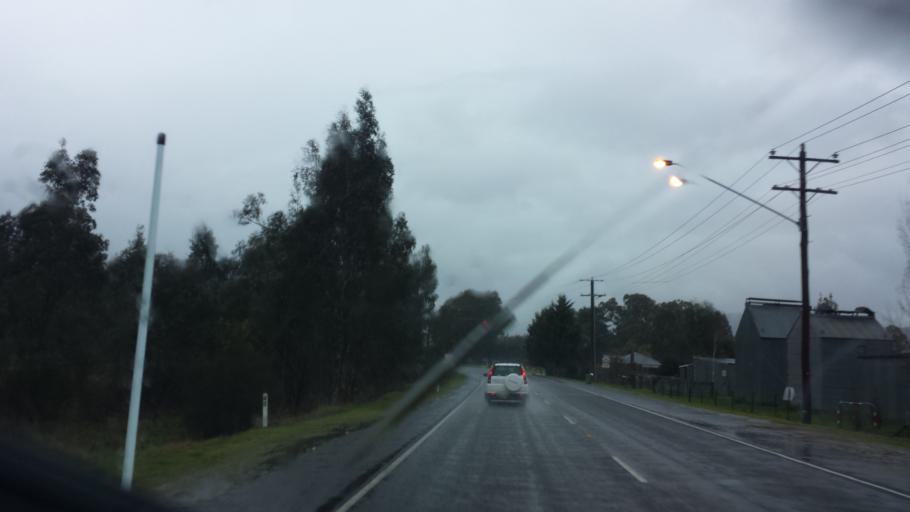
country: AU
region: Victoria
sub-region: Alpine
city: Mount Beauty
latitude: -36.5867
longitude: 146.7593
